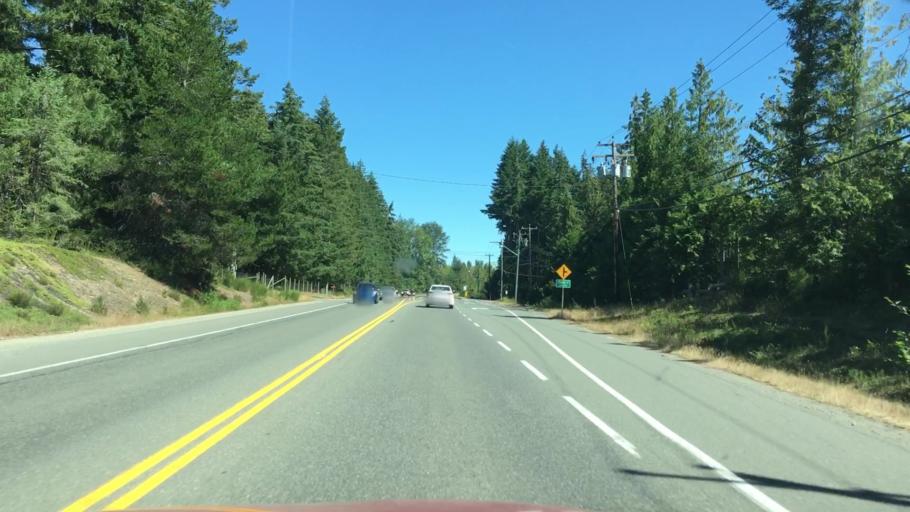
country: CA
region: British Columbia
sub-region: Regional District of Nanaimo
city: Parksville
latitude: 49.3110
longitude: -124.5012
